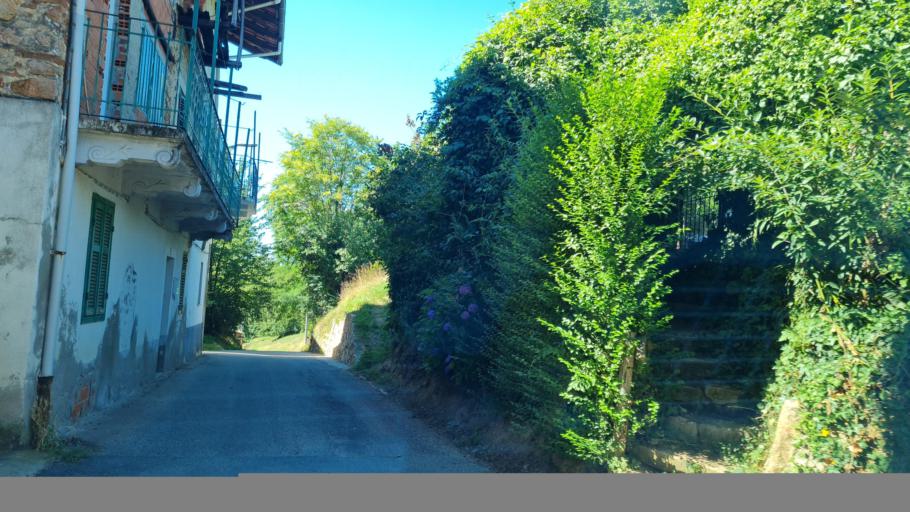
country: IT
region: Piedmont
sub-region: Provincia di Biella
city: Masserano
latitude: 45.5868
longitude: 8.2202
